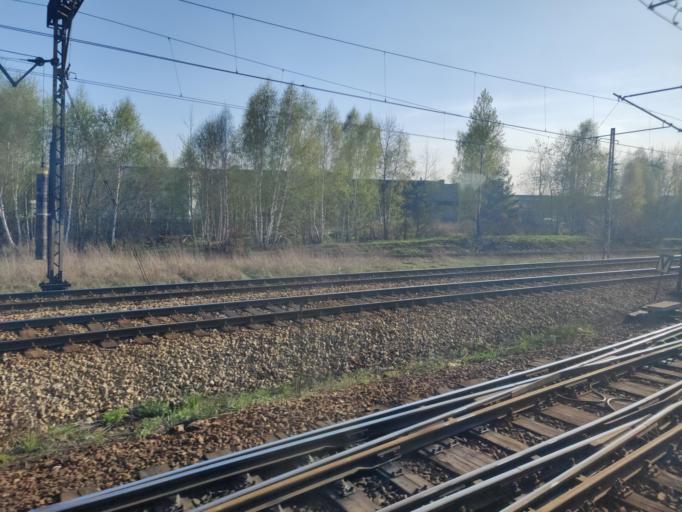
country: PL
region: Silesian Voivodeship
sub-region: Katowice
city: Katowice
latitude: 50.2565
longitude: 19.0674
